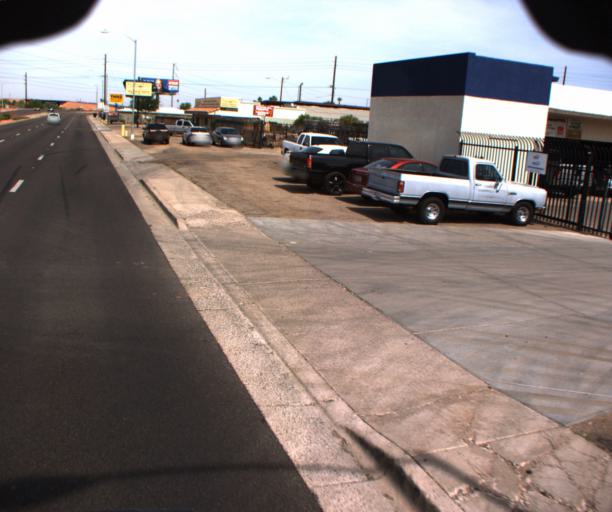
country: US
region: Arizona
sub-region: Maricopa County
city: Glendale
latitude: 33.5584
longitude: -112.2094
